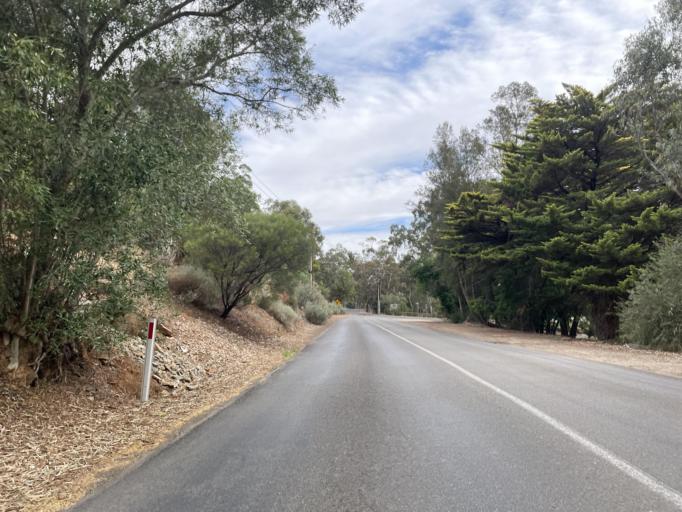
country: AU
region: South Australia
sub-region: Clare and Gilbert Valleys
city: Clare
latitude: -33.8415
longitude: 138.6132
